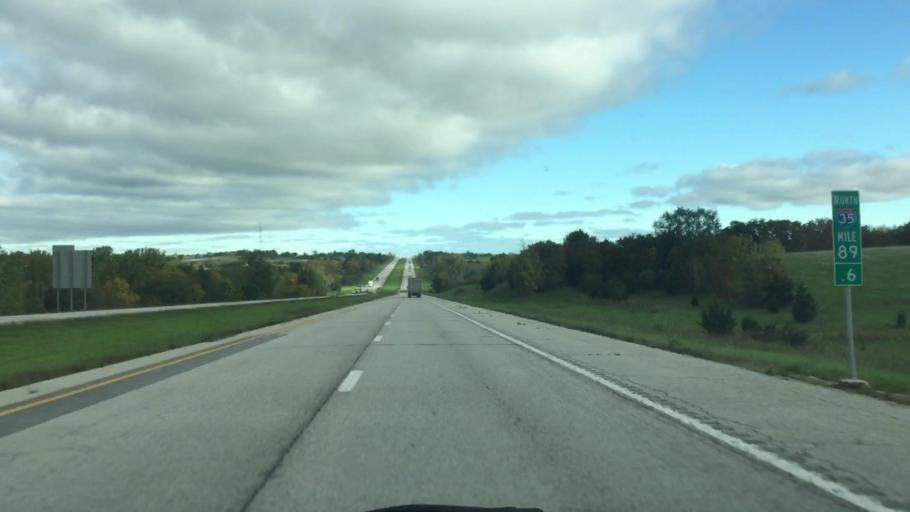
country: US
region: Missouri
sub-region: Harrison County
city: Bethany
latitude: 40.2274
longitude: -94.0128
